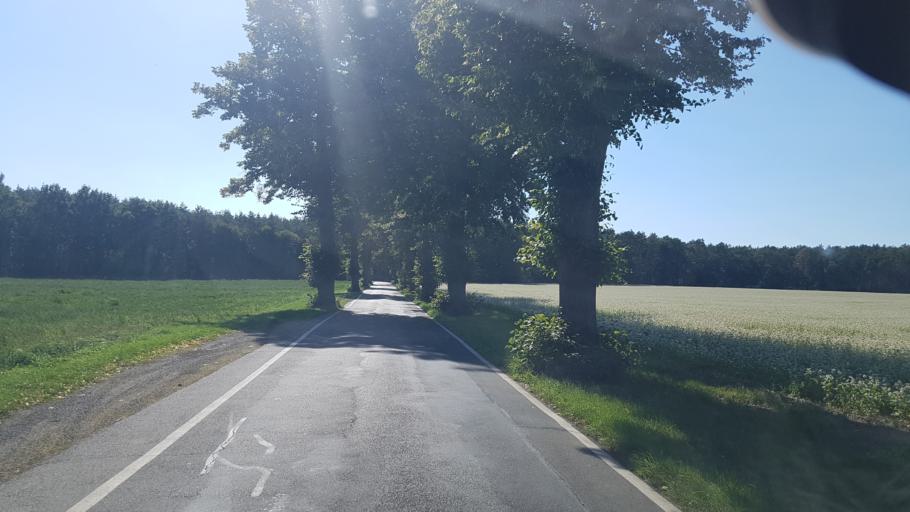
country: DE
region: Brandenburg
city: Hirschfeld
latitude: 51.3763
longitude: 13.5969
